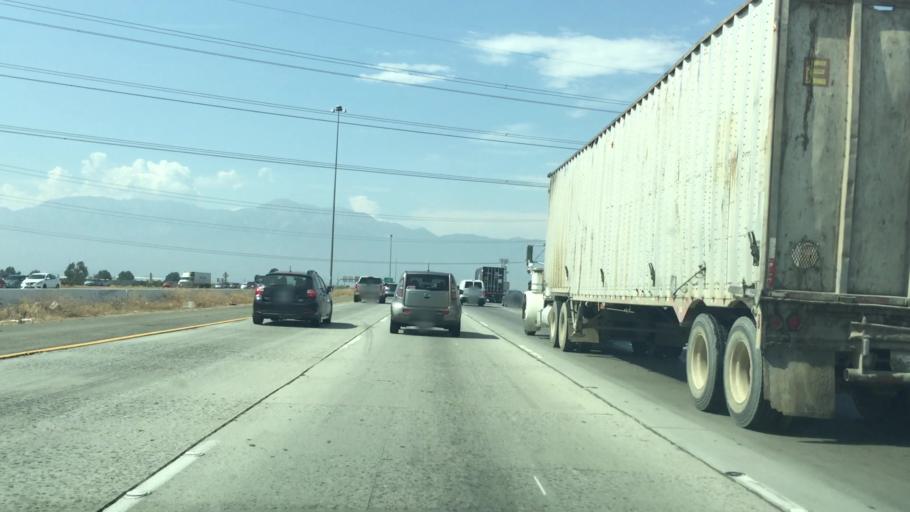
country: US
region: California
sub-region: Riverside County
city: Mira Loma
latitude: 34.0261
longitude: -117.5501
